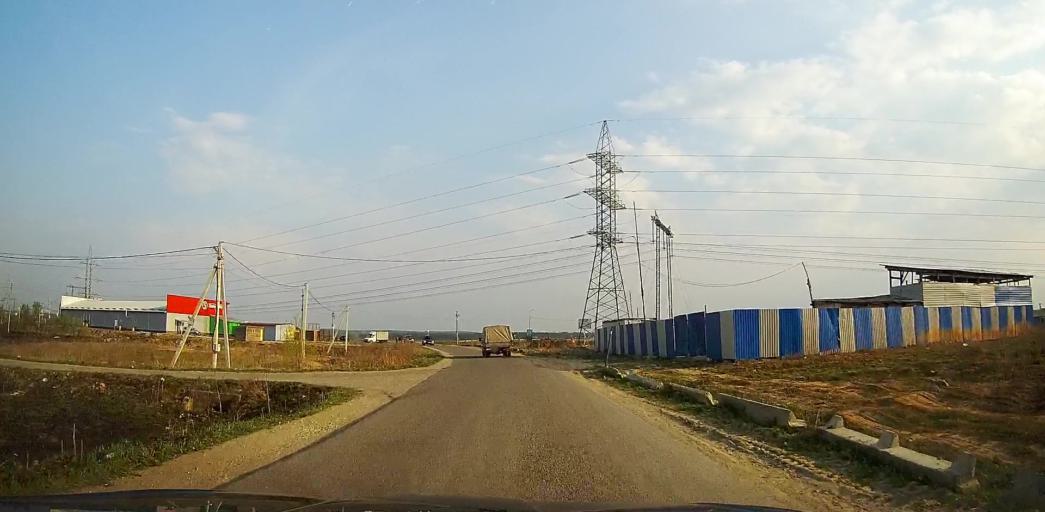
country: RU
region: Moskovskaya
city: Andreyevskoye
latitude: 55.5369
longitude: 37.9701
